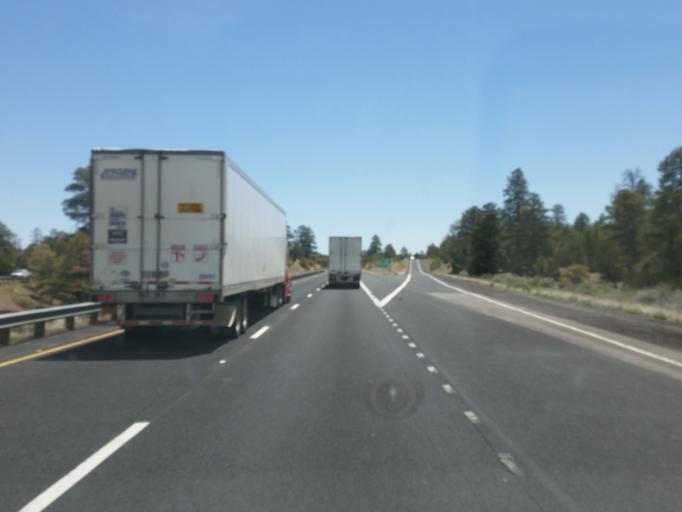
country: US
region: Arizona
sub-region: Coconino County
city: Flagstaff
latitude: 35.2096
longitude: -111.5225
